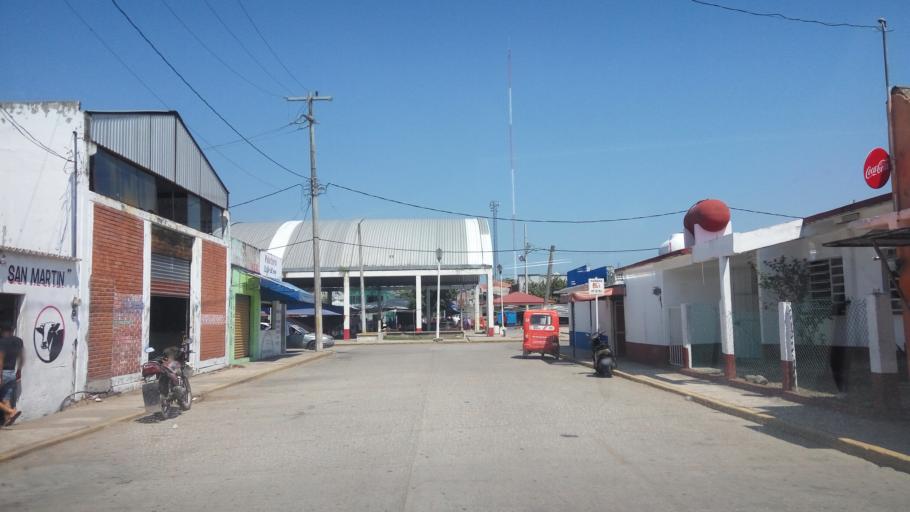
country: MX
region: Tabasco
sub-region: Centla
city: Ignacio Zaragoza
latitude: 18.4014
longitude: -92.9560
